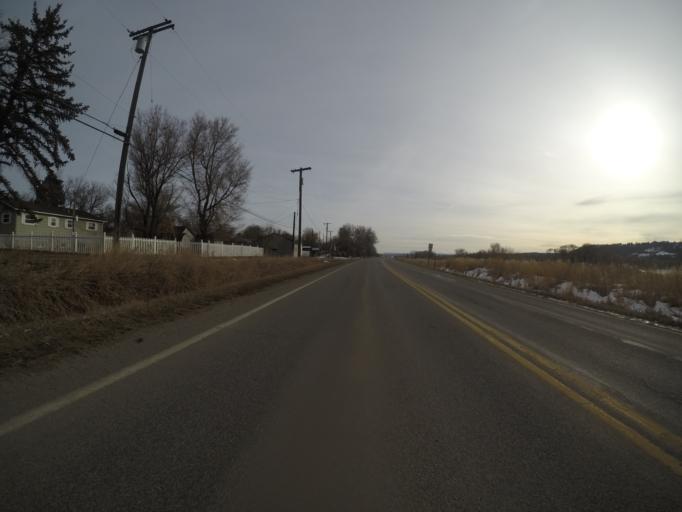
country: US
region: Montana
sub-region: Stillwater County
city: Columbus
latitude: 45.6398
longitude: -109.2637
